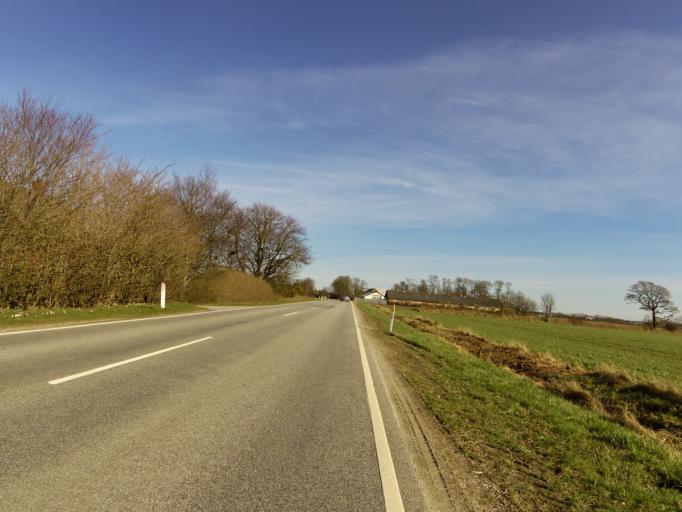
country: DK
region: South Denmark
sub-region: Vejen Kommune
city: Rodding
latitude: 55.3624
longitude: 9.1087
